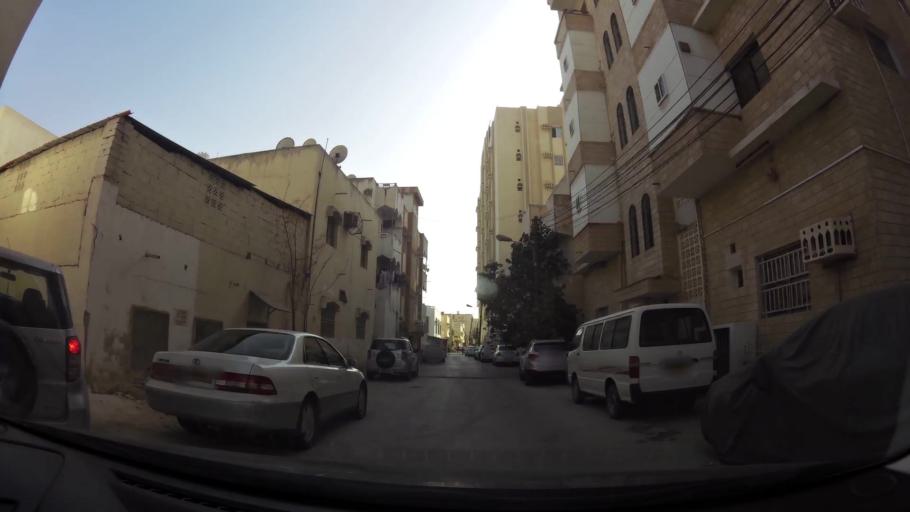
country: OM
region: Zufar
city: Salalah
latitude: 17.0127
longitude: 54.0853
